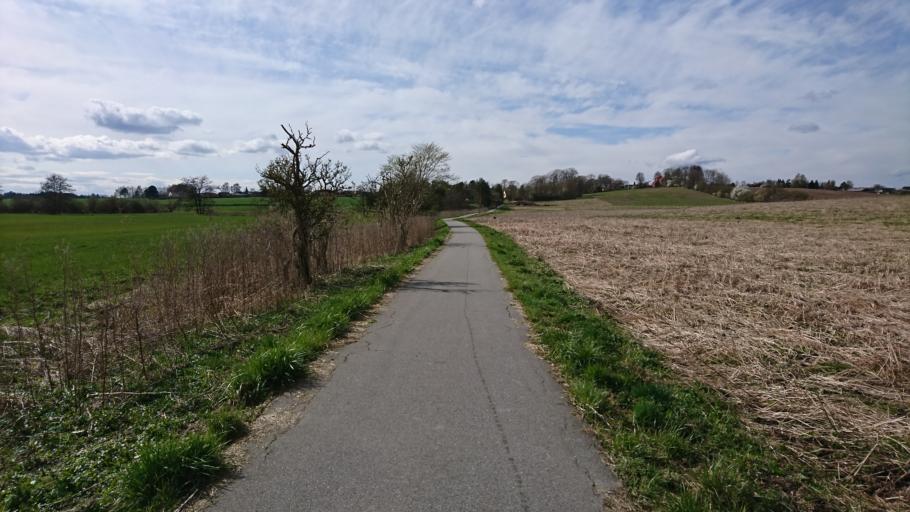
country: DK
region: Capital Region
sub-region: Egedal Kommune
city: Ganlose
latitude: 55.7967
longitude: 12.2345
